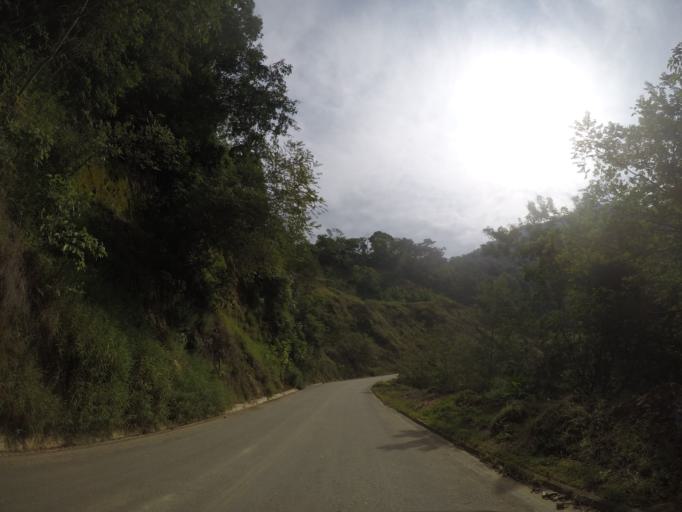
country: MX
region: Oaxaca
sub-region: San Pedro Pochutla
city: Los Naranjos Esquipulas
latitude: 15.9528
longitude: -96.4490
